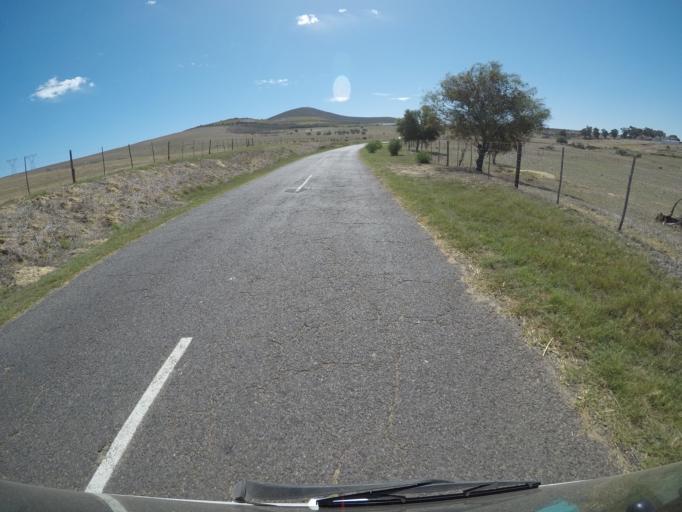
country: ZA
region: Western Cape
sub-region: City of Cape Town
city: Sunset Beach
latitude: -33.7305
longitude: 18.5650
